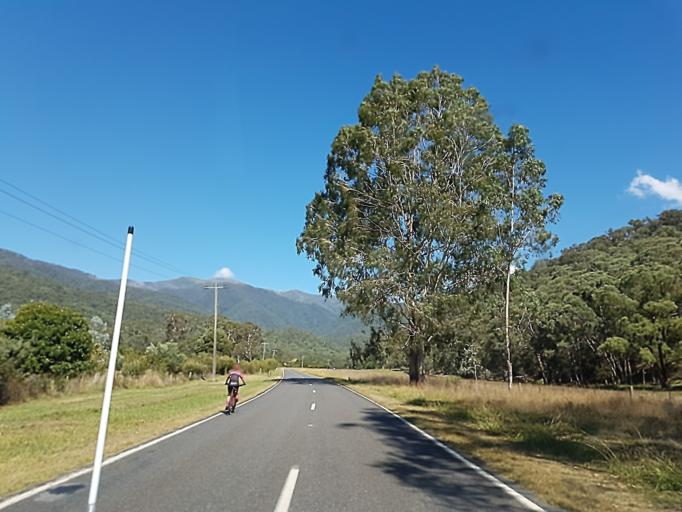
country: AU
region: Victoria
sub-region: Alpine
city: Mount Beauty
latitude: -36.8332
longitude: 147.0744
